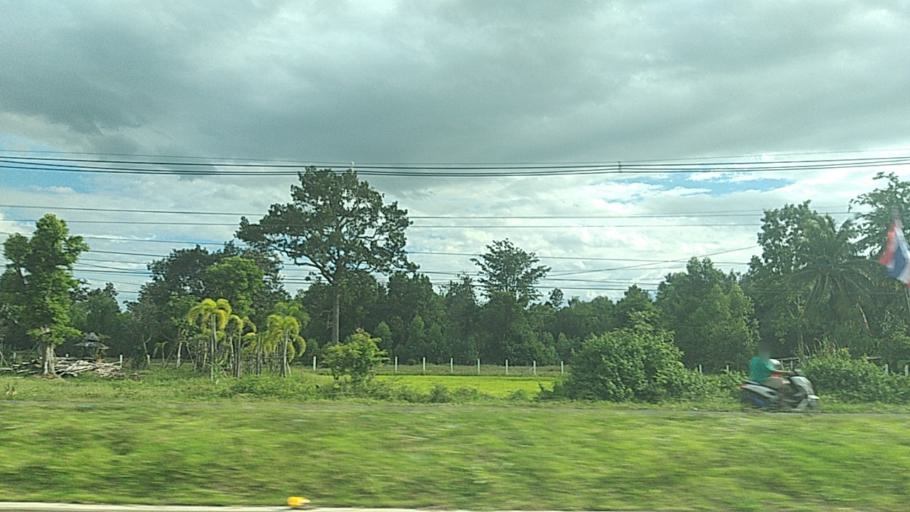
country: TH
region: Surin
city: Prasat
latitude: 14.6044
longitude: 103.4276
